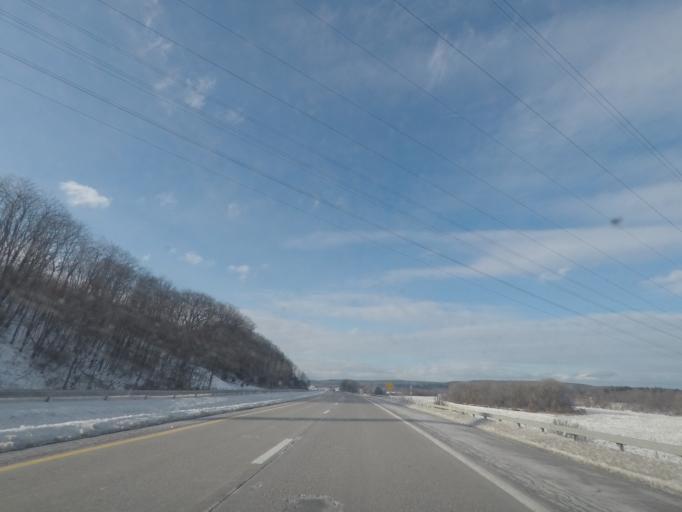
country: US
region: New York
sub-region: Schenectady County
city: Scotia
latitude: 42.8324
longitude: -73.9951
